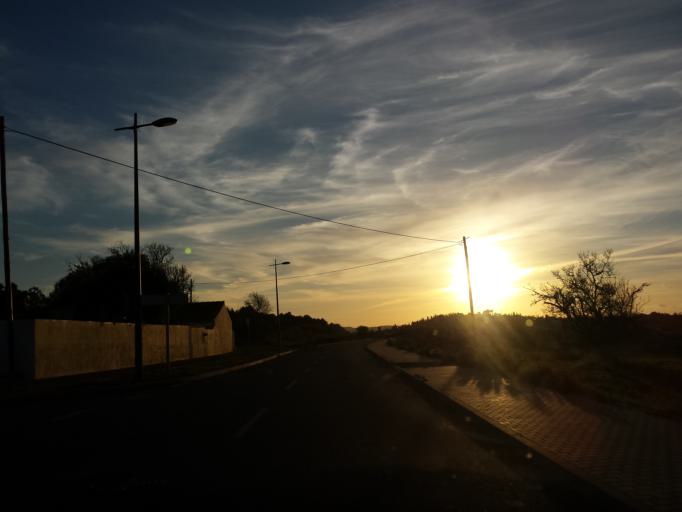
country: PT
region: Faro
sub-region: Lagos
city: Lagos
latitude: 37.1259
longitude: -8.6515
